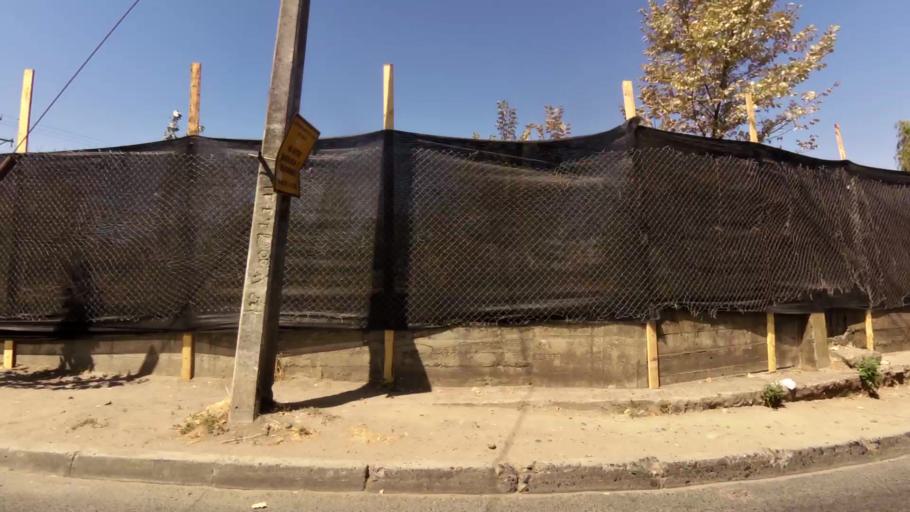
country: CL
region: Maule
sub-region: Provincia de Talca
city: Talca
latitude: -35.4159
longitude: -71.6492
